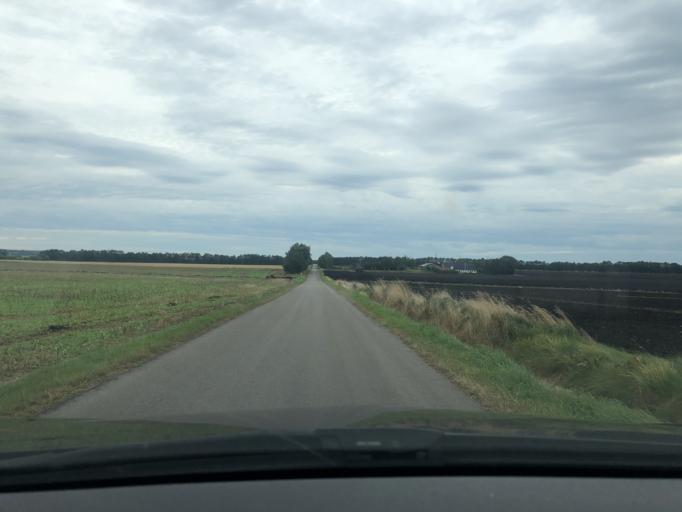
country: DK
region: South Denmark
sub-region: Varde Kommune
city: Olgod
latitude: 55.7974
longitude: 8.6904
